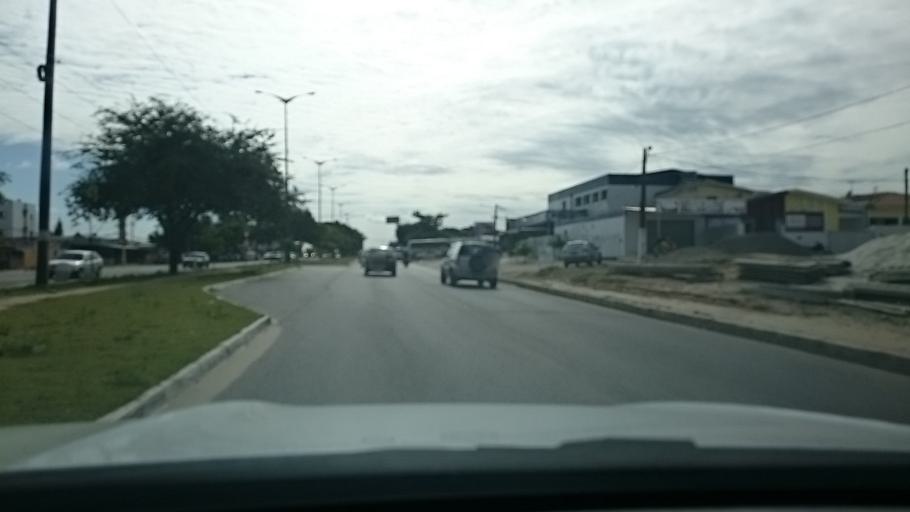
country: BR
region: Paraiba
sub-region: Joao Pessoa
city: Joao Pessoa
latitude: -7.1683
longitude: -34.8570
